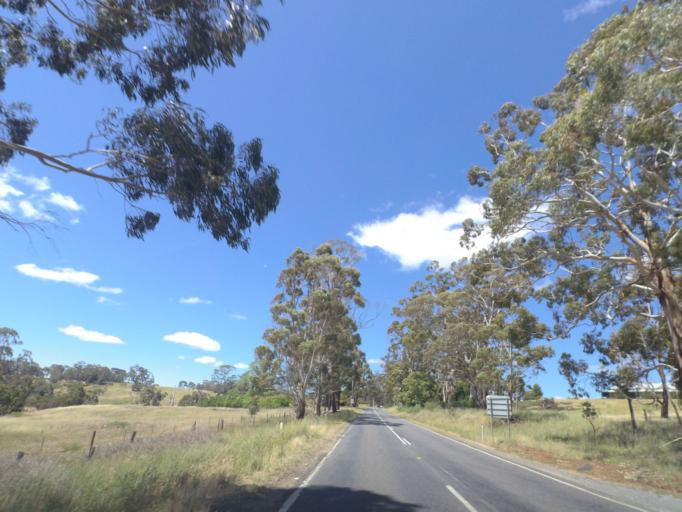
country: AU
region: Victoria
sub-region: Mount Alexander
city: Castlemaine
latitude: -37.2923
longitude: 144.2479
